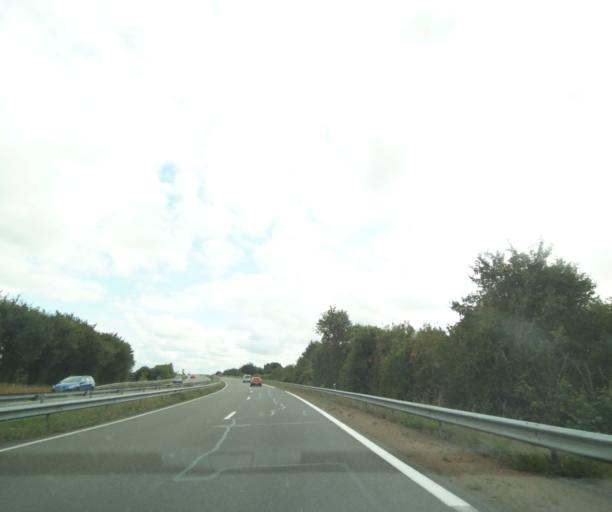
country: FR
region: Pays de la Loire
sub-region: Departement de la Vendee
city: Saligny
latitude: 46.8395
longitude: -1.4197
